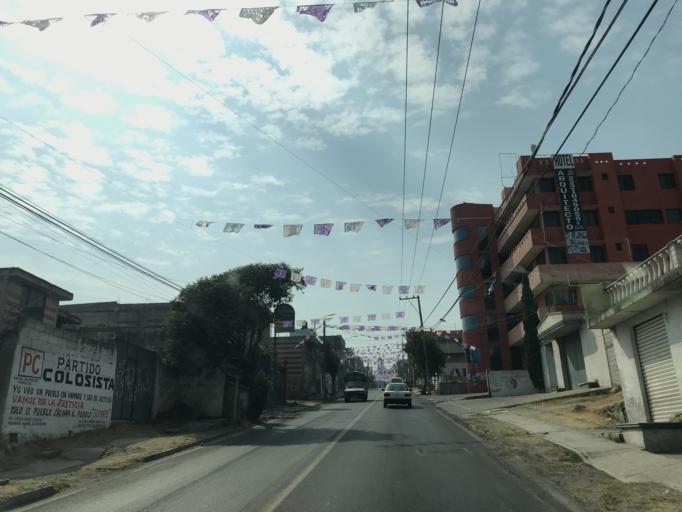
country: MX
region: Tlaxcala
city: Tenancingo
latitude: 19.1493
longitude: -98.2037
